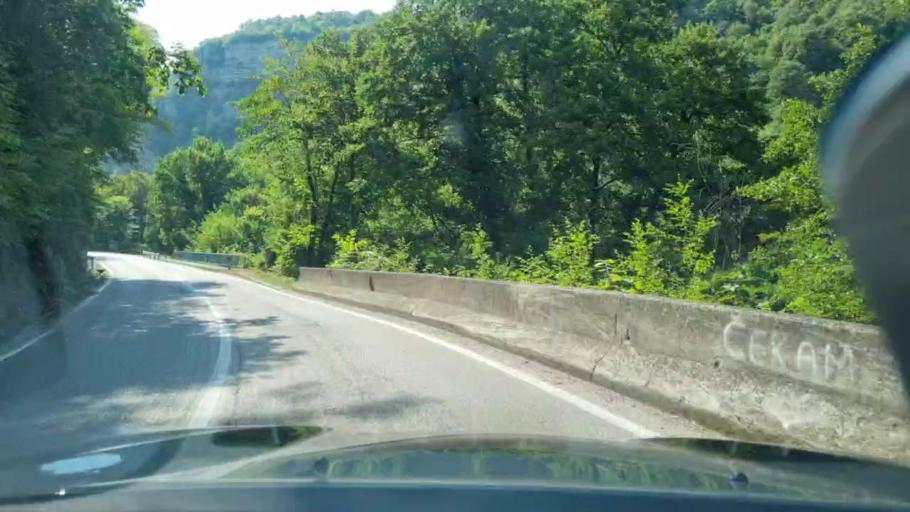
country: BA
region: Federation of Bosnia and Herzegovina
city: Bosanska Krupa
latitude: 44.8703
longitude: 16.1039
